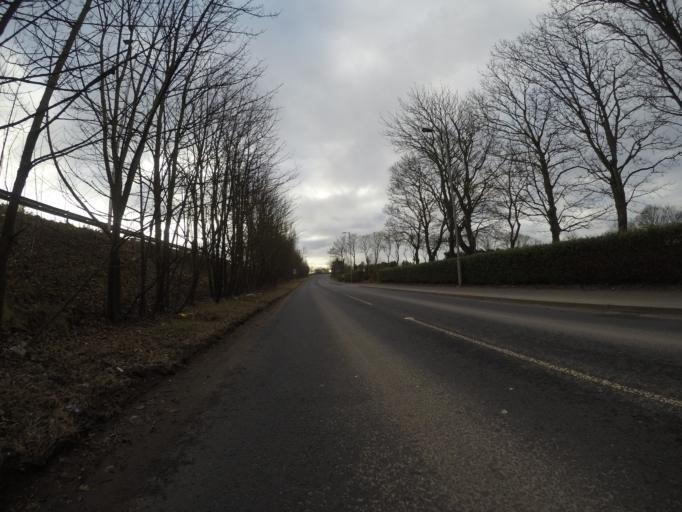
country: GB
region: Scotland
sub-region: South Ayrshire
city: Troon
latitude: 55.5712
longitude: -4.6397
